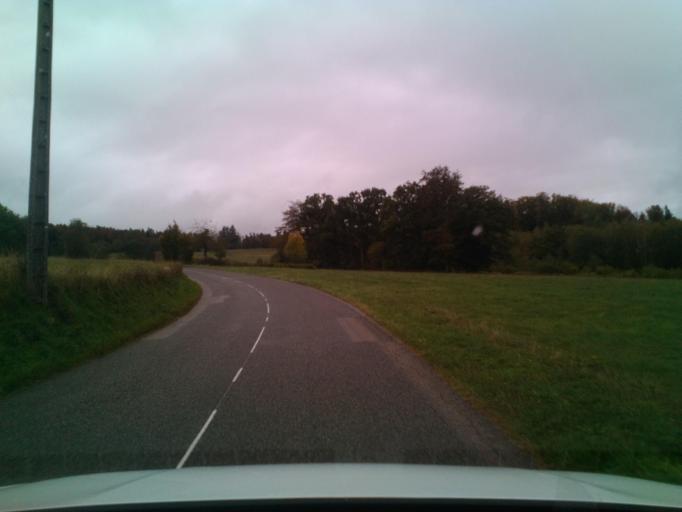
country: FR
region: Lorraine
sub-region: Departement des Vosges
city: Senones
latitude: 48.3649
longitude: 6.9684
